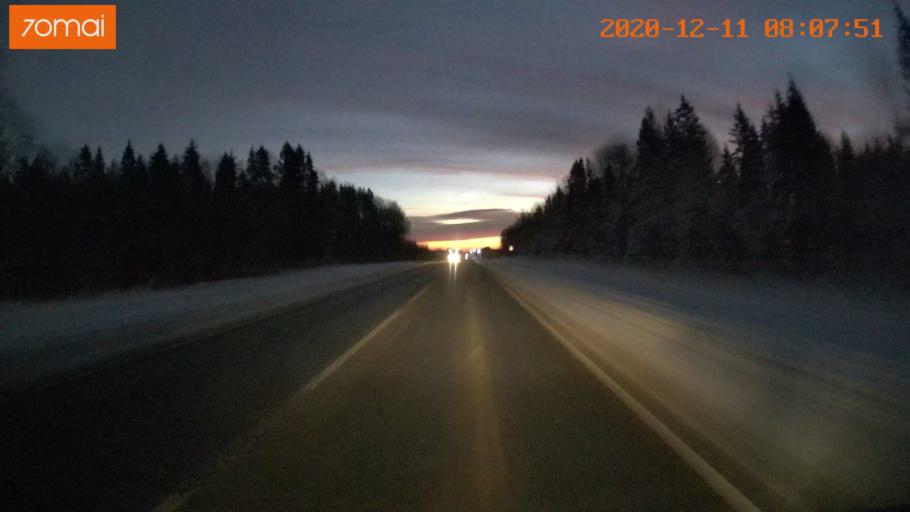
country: RU
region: Vologda
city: Chebsara
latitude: 59.1201
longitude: 39.0826
